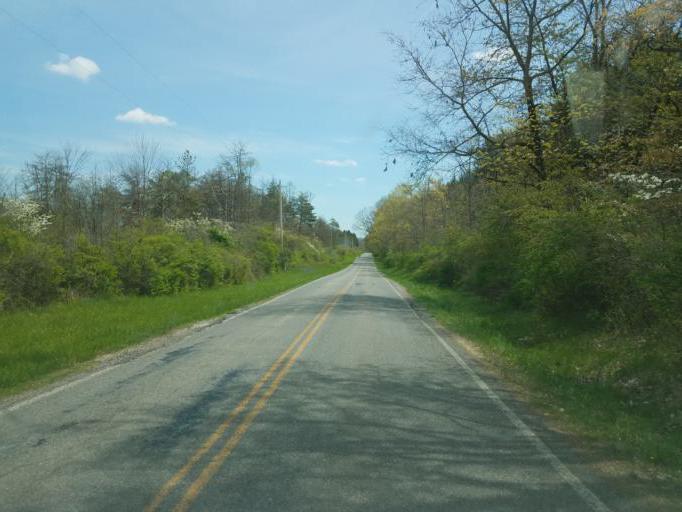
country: US
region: Ohio
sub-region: Summit County
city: Peninsula
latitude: 41.2331
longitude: -81.5635
